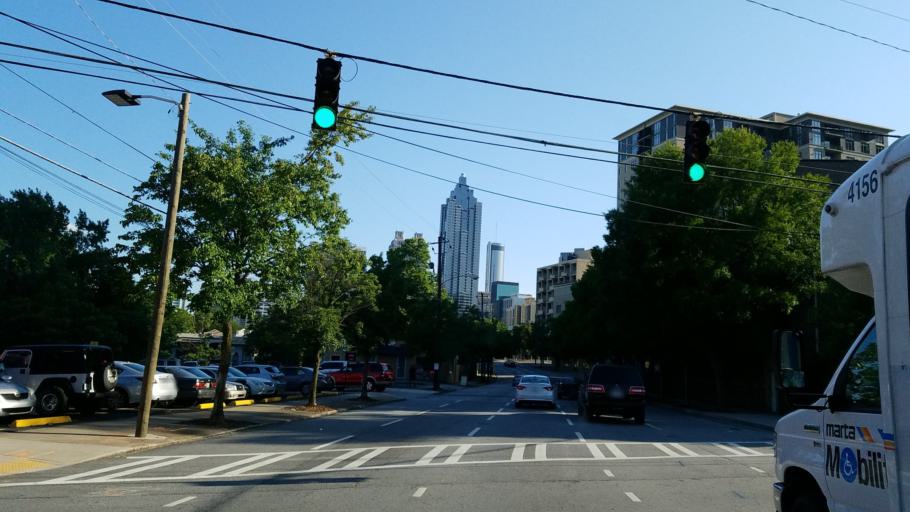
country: US
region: Georgia
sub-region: Fulton County
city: Atlanta
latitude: 33.7713
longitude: -84.3834
